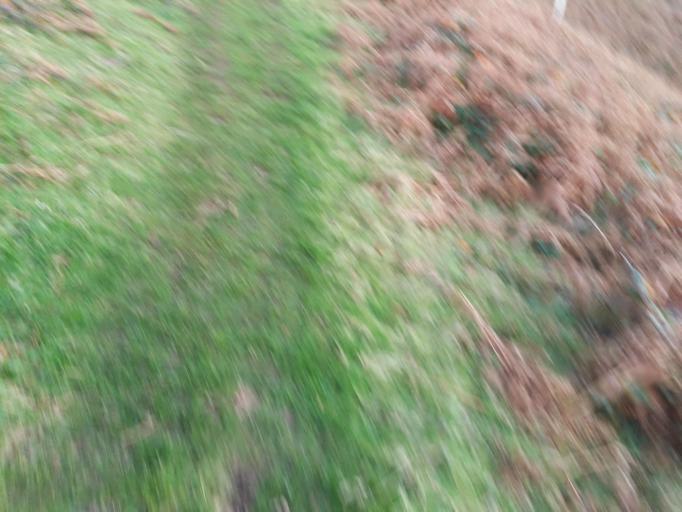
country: GB
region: England
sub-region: Cornwall
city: Fowey
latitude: 50.3272
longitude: -4.6007
